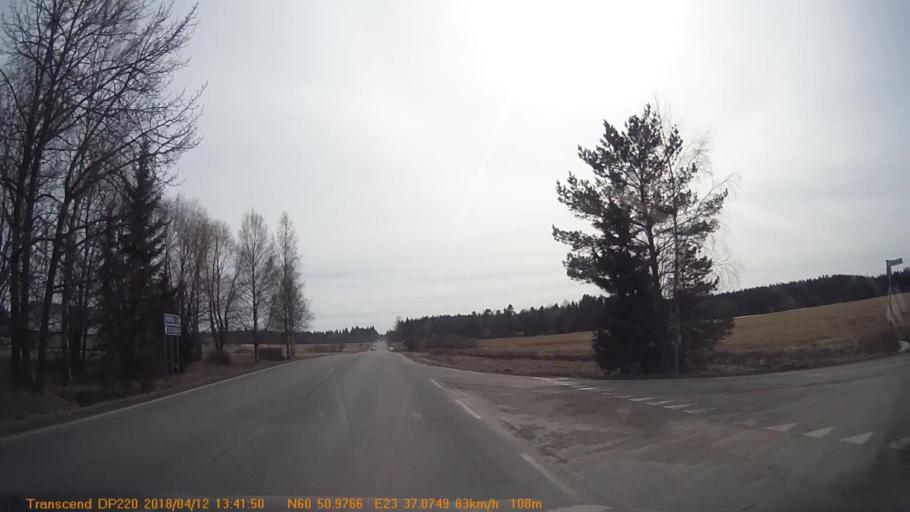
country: FI
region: Haeme
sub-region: Forssa
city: Forssa
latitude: 60.8489
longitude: 23.6179
